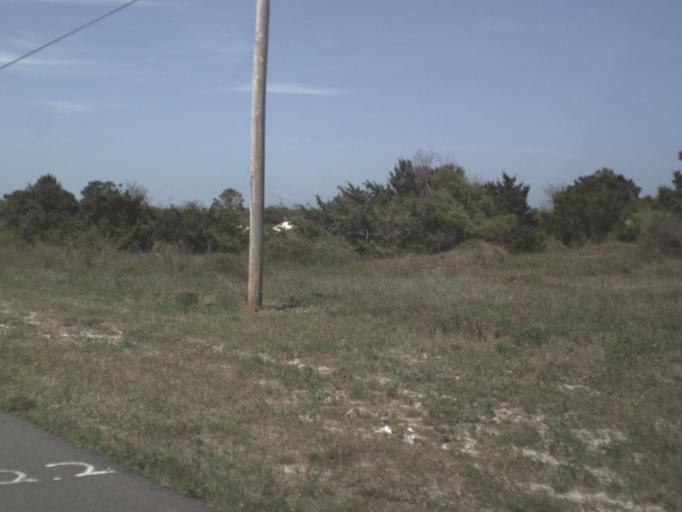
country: US
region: Florida
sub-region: Duval County
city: Atlantic Beach
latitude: 30.4509
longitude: -81.4156
